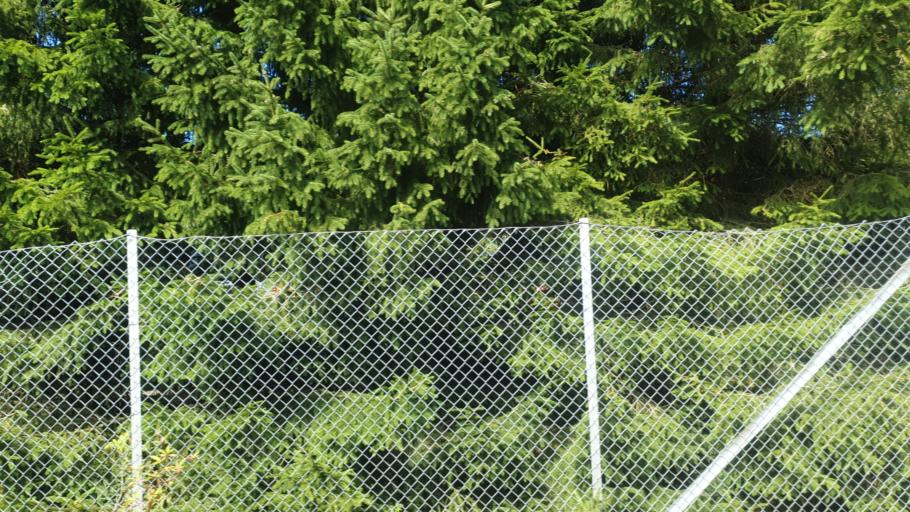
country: NO
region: Sor-Trondelag
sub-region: Orkdal
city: Orkanger
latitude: 63.2773
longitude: 9.8255
